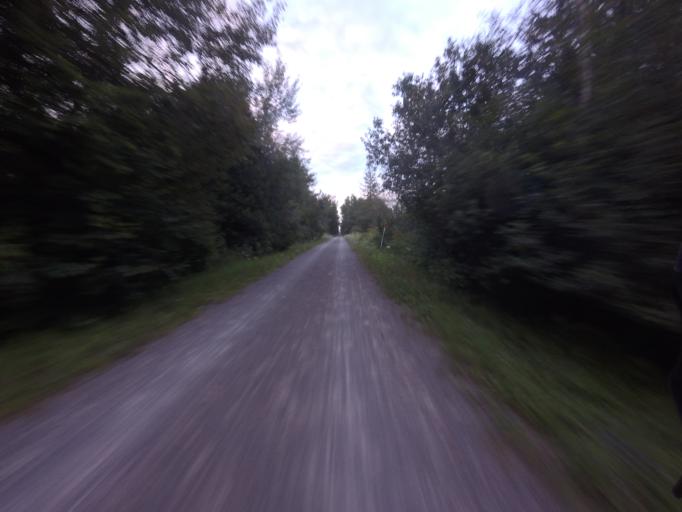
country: CA
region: Ontario
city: Carleton Place
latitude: 45.2143
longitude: -75.9904
